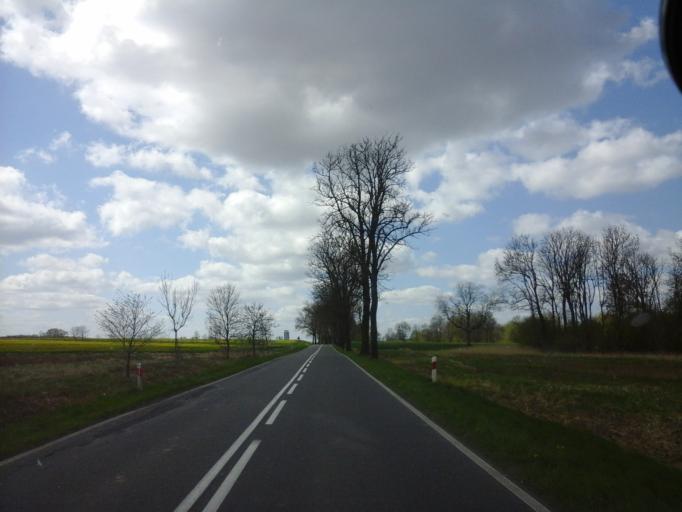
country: PL
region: West Pomeranian Voivodeship
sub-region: Powiat choszczenski
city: Choszczno
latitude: 53.1728
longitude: 15.4732
